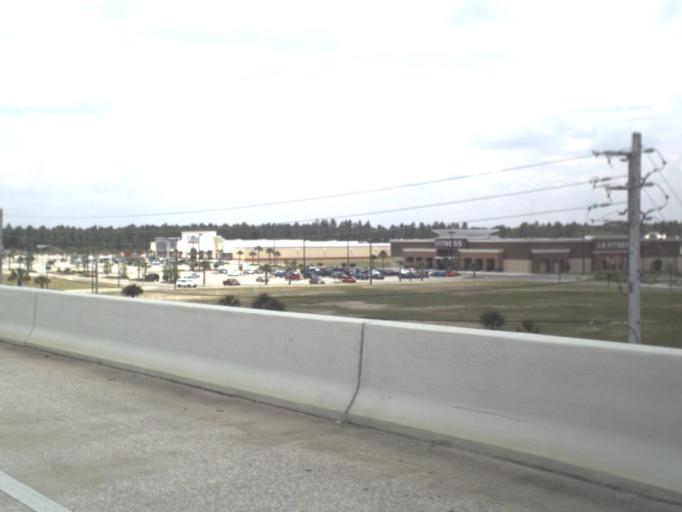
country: US
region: Florida
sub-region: Duval County
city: Atlantic Beach
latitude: 30.3198
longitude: -81.4898
